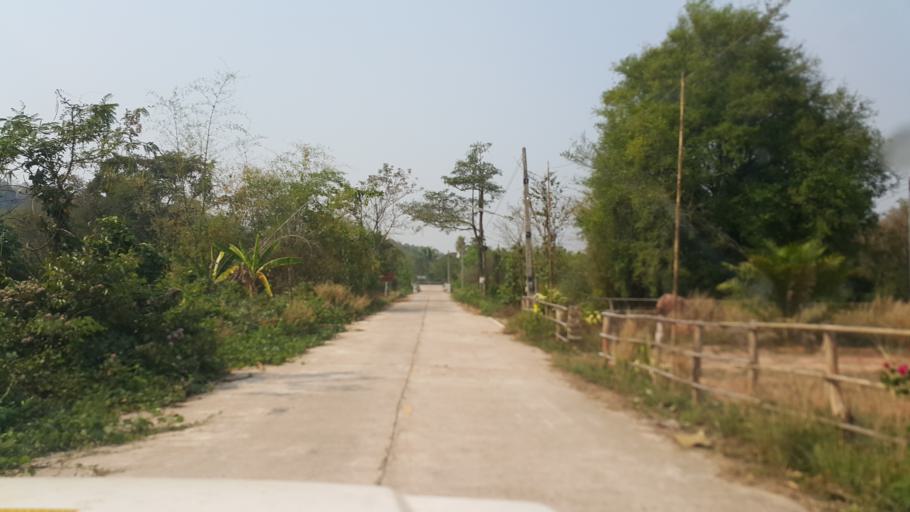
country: TH
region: Nakhon Phanom
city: Ban Phaeng
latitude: 17.9847
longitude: 104.1455
